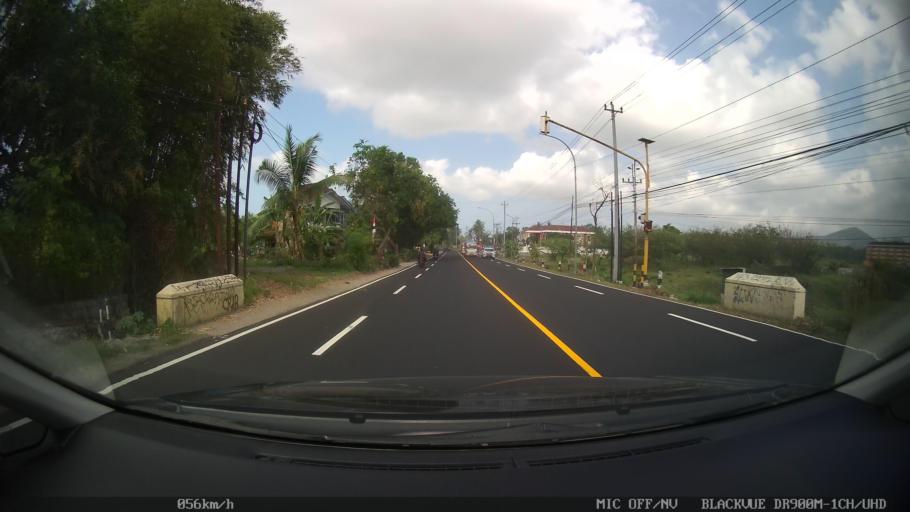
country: ID
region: Daerah Istimewa Yogyakarta
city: Srandakan
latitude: -7.8728
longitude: 110.1387
